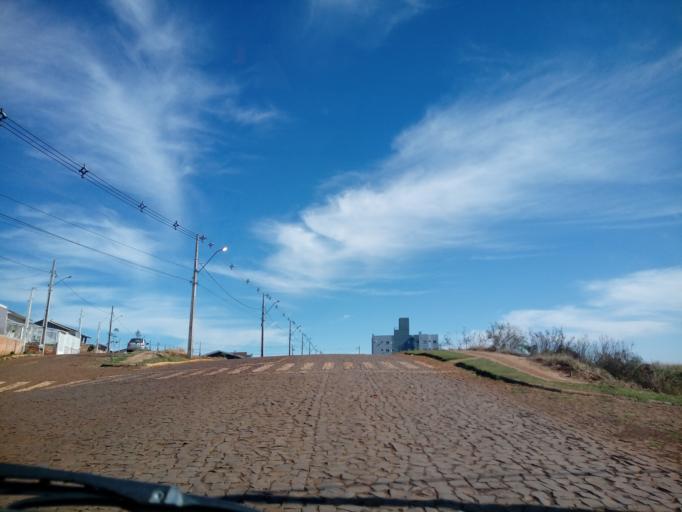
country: BR
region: Santa Catarina
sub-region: Chapeco
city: Chapeco
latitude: -27.0387
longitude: -52.6197
